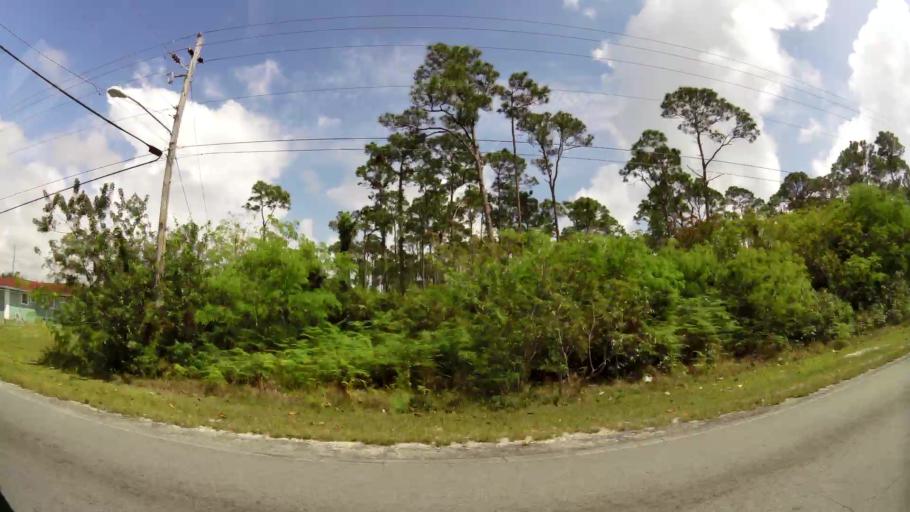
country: BS
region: Freeport
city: Freeport
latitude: 26.5078
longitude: -78.6911
